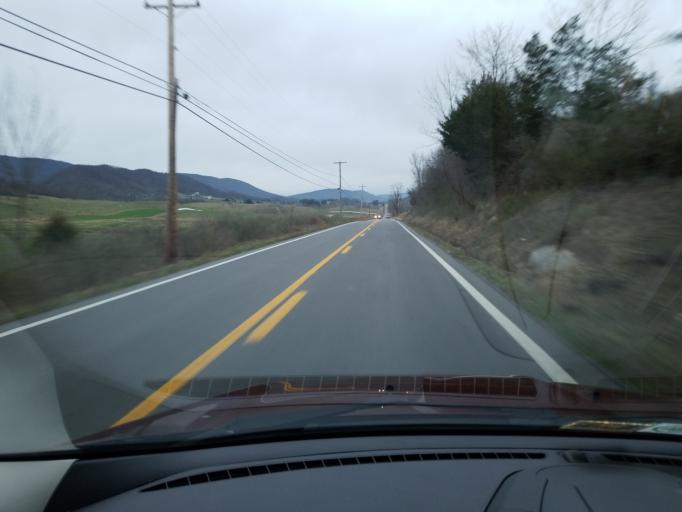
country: US
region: Virginia
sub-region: Giles County
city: Pearisburg
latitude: 37.4249
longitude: -80.7298
